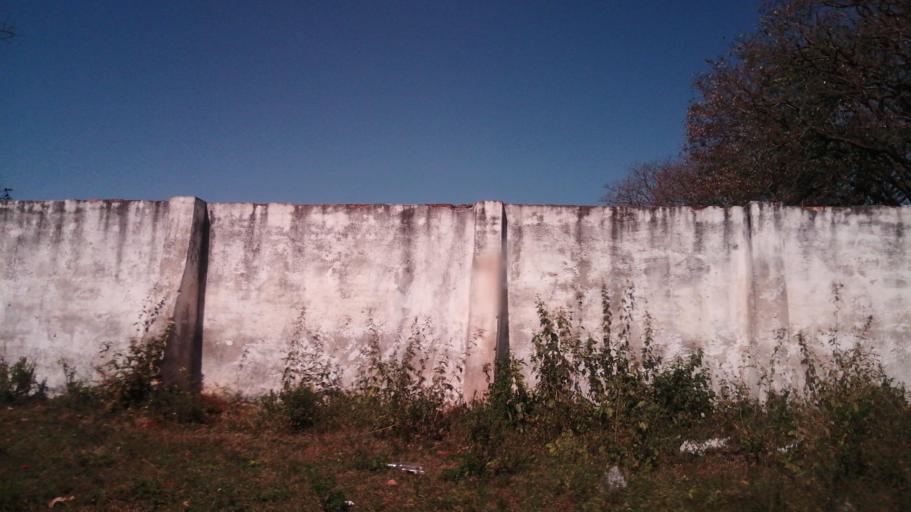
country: PY
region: Misiones
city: San Juan Bautista
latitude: -26.6652
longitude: -57.1549
